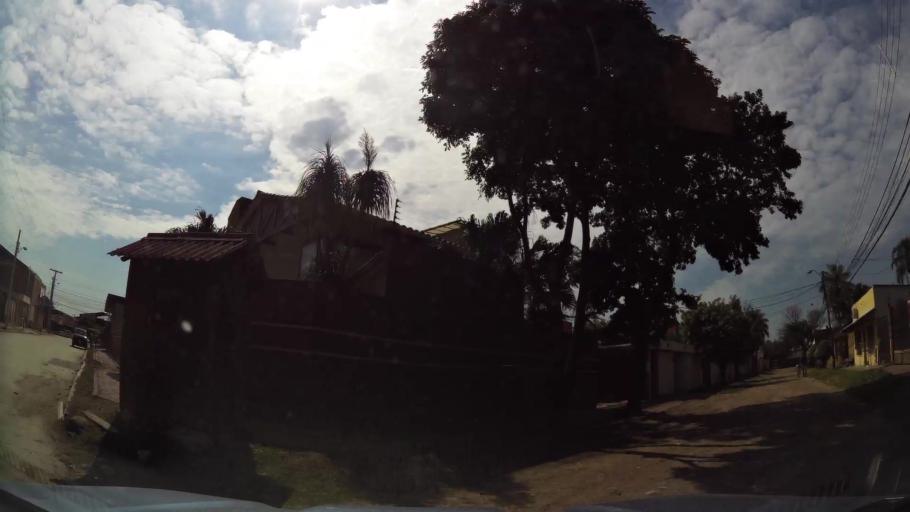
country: BO
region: Santa Cruz
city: Santa Cruz de la Sierra
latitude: -17.7470
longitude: -63.1567
